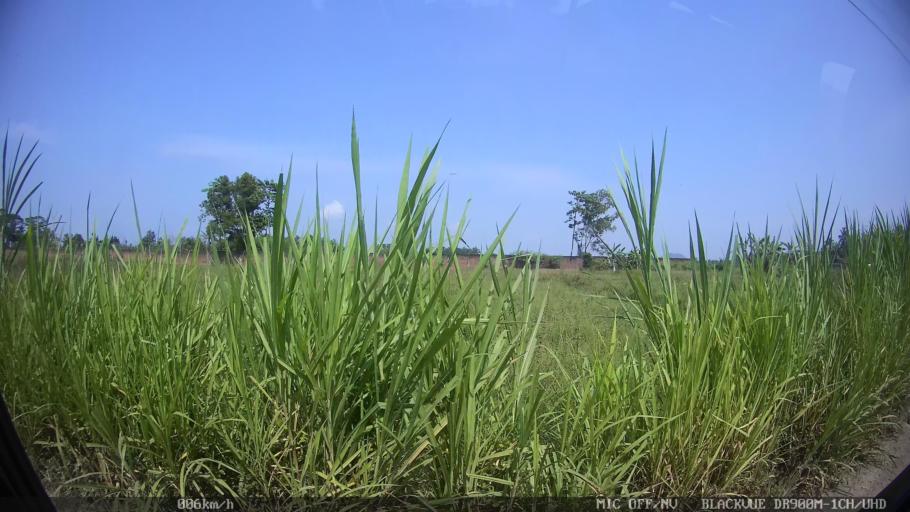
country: ID
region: Lampung
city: Natar
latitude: -5.2623
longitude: 105.1973
